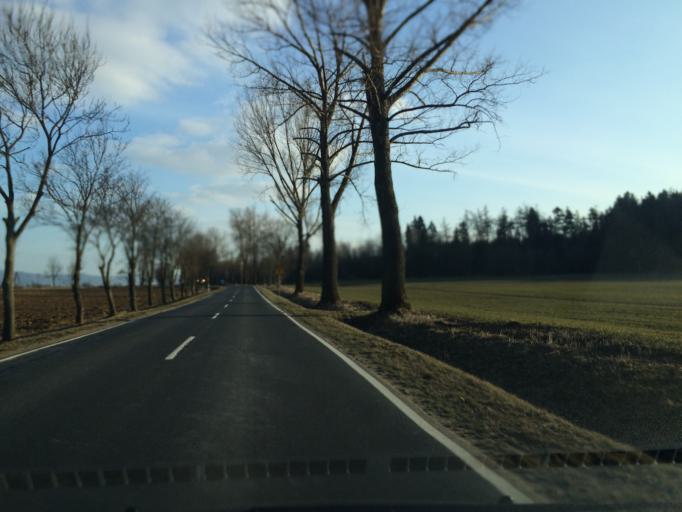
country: PL
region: Lower Silesian Voivodeship
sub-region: Powiat klodzki
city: Bystrzyca Klodzka
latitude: 50.2399
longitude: 16.6738
